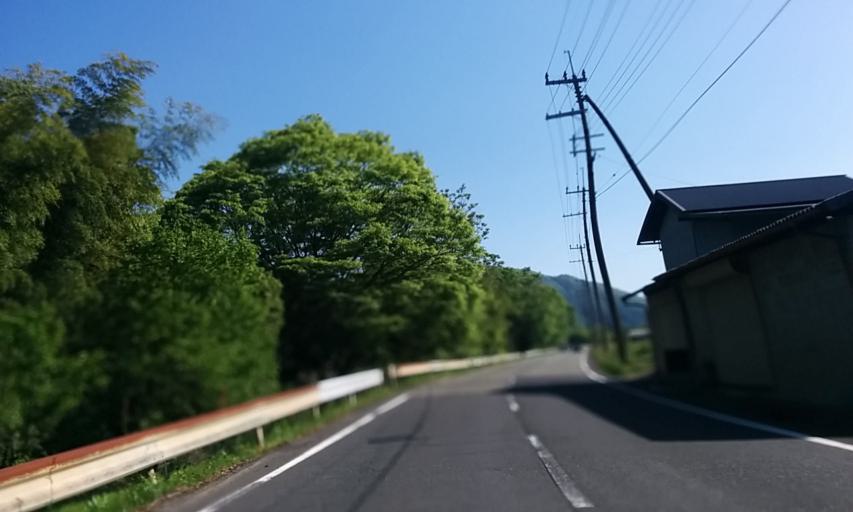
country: JP
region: Kyoto
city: Ayabe
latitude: 35.2612
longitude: 135.4291
